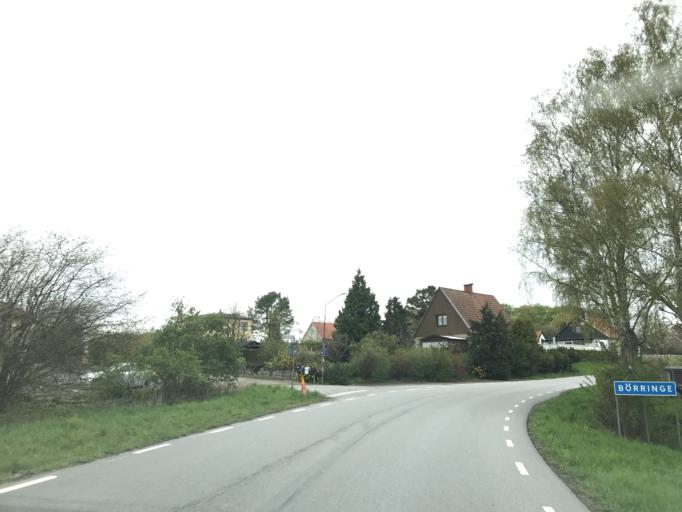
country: SE
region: Skane
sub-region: Trelleborgs Kommun
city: Anderslov
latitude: 55.4960
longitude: 13.3324
